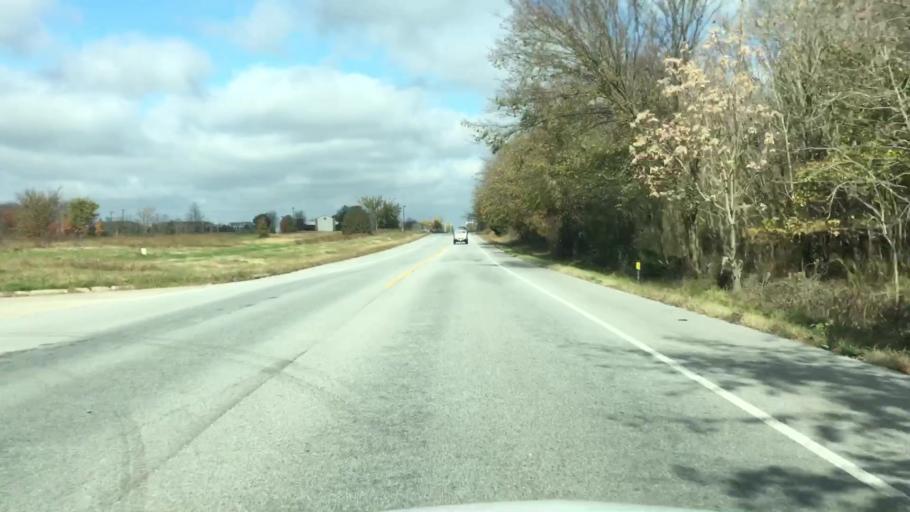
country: US
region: Arkansas
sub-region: Benton County
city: Centerton
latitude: 36.3051
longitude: -94.3039
